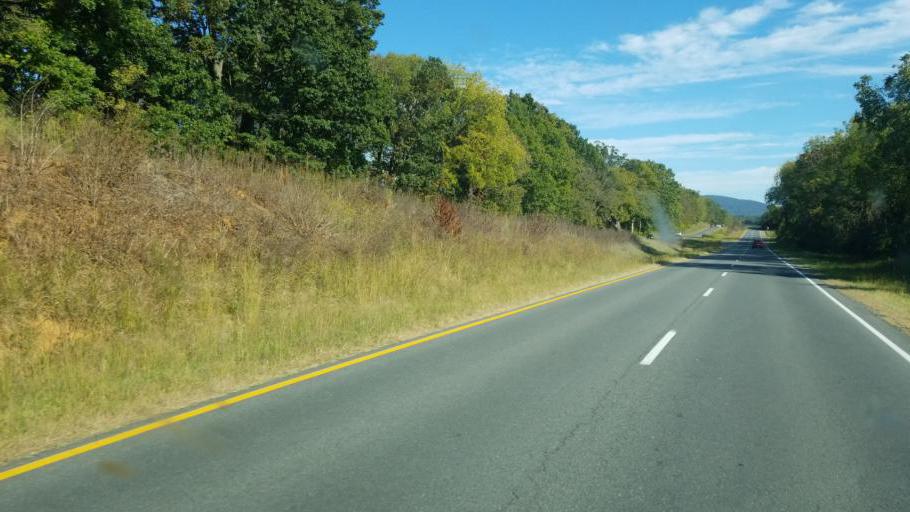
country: US
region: Virginia
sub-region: Warren County
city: Shenandoah Farms
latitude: 39.0647
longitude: -78.0526
